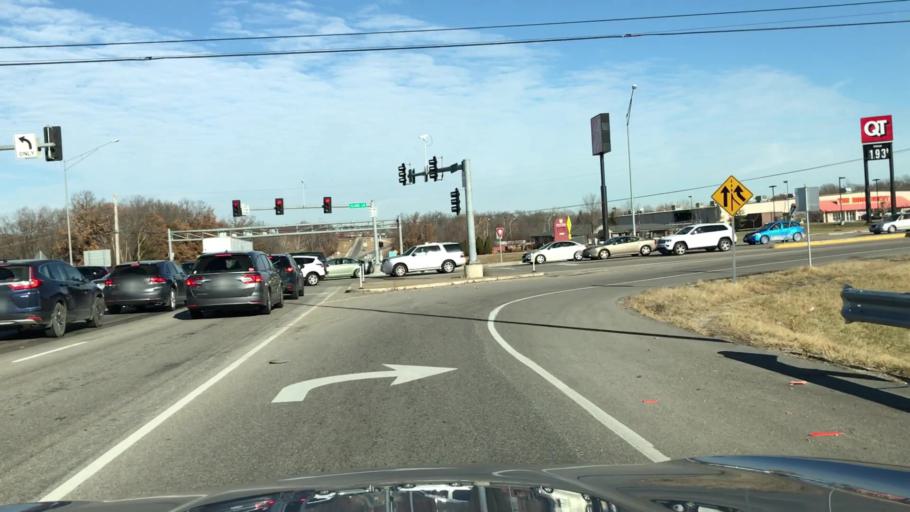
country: US
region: Missouri
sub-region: Boone County
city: Columbia
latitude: 38.9633
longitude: -92.2918
